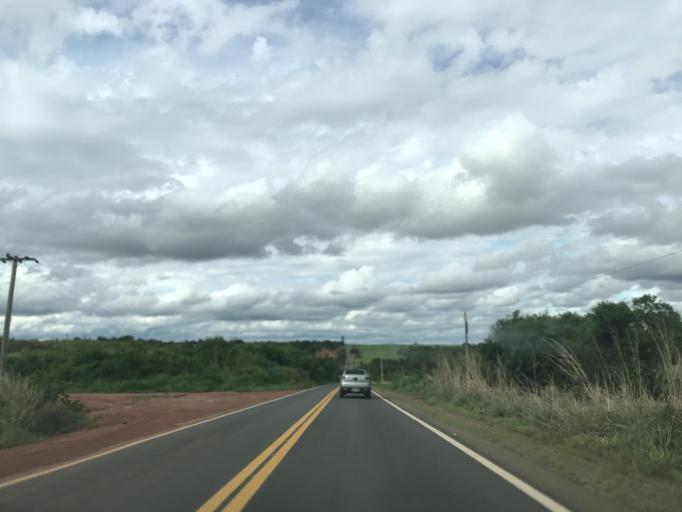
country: BR
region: Goias
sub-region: Piracanjuba
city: Piracanjuba
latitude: -17.1989
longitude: -48.7009
